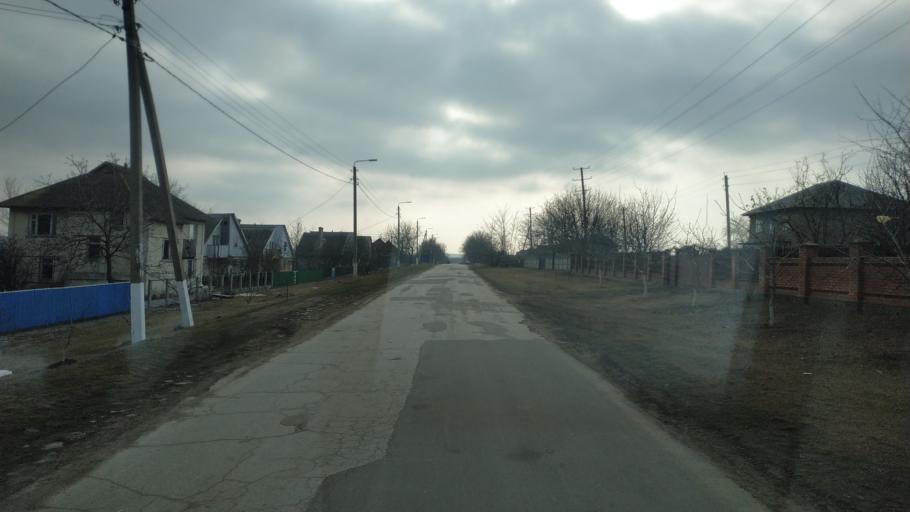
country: MD
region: Hincesti
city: Dancu
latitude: 46.8182
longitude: 28.2725
